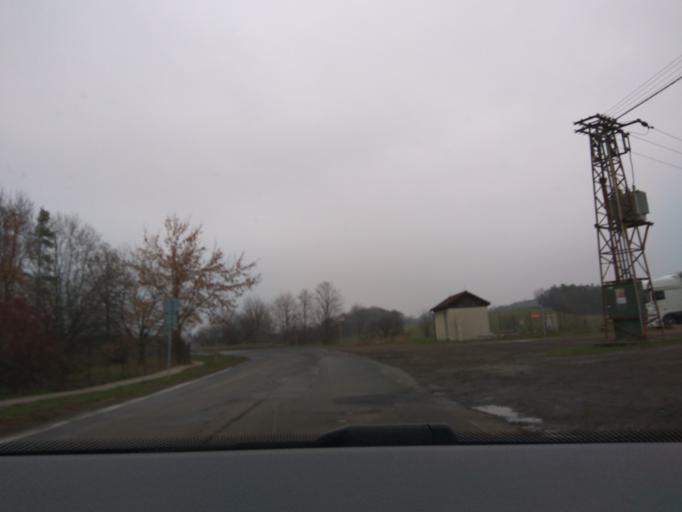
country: CZ
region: Central Bohemia
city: Hovorcovice
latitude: 50.1687
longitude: 14.5441
